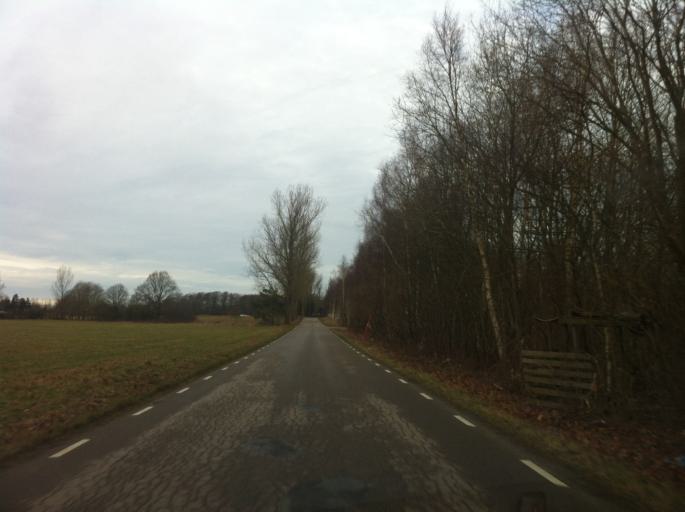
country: SE
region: Skane
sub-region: Astorps Kommun
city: Kvidinge
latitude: 56.0921
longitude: 13.0936
